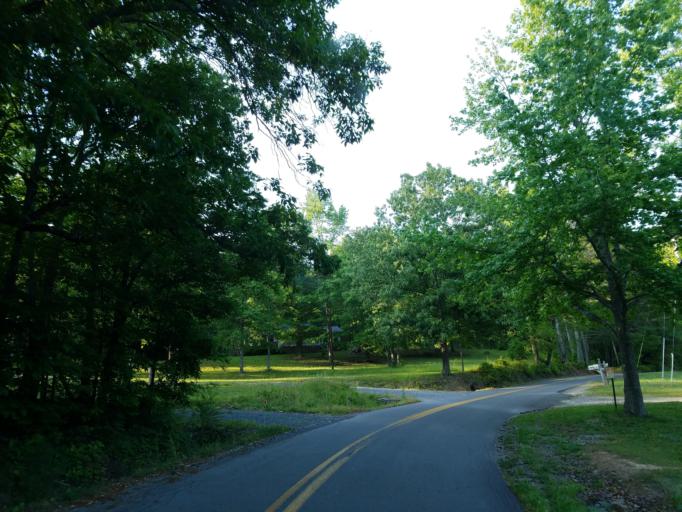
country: US
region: Georgia
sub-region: Gordon County
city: Calhoun
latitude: 34.5496
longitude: -85.1079
